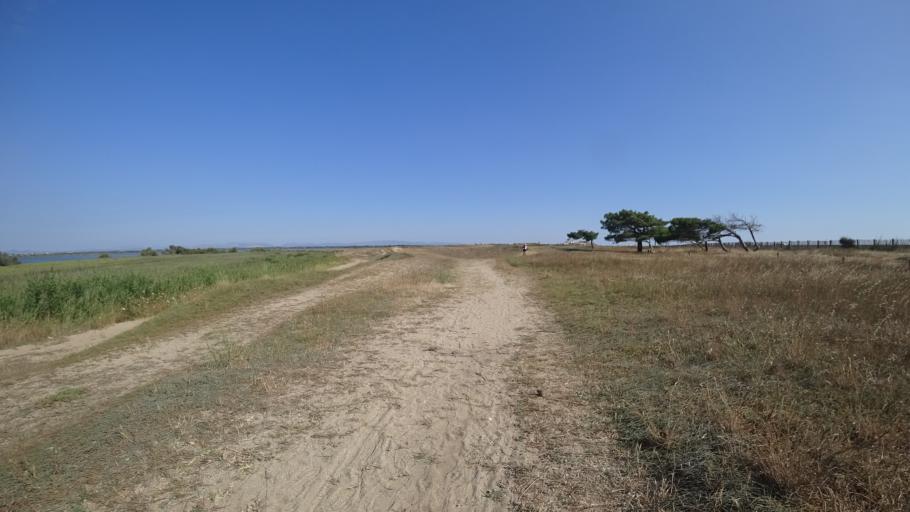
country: FR
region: Languedoc-Roussillon
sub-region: Departement des Pyrenees-Orientales
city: Saint-Cyprien-Plage
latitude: 42.6624
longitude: 3.0318
